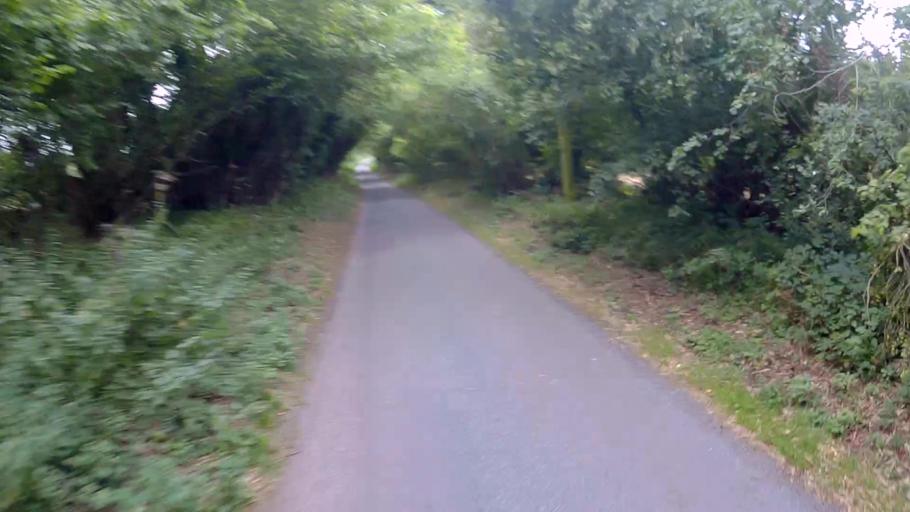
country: GB
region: England
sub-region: Hampshire
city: Overton
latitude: 51.2177
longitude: -1.2252
